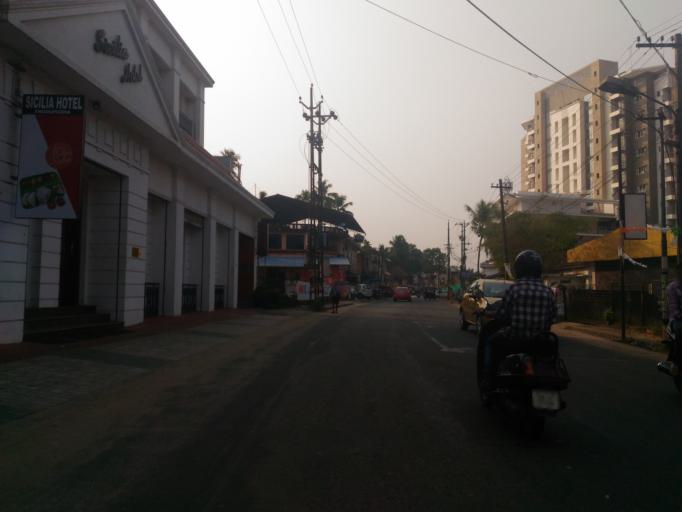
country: IN
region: Kerala
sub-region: Ernakulam
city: Muvattupula
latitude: 9.8944
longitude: 76.7142
